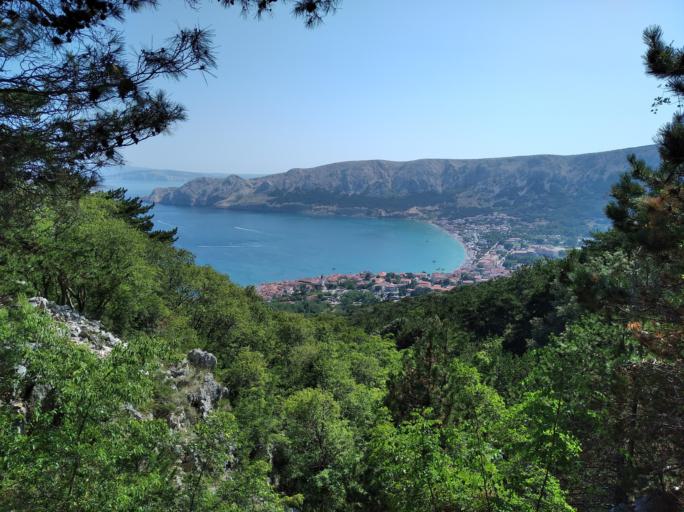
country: HR
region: Primorsko-Goranska
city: Punat
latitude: 44.9779
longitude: 14.7594
